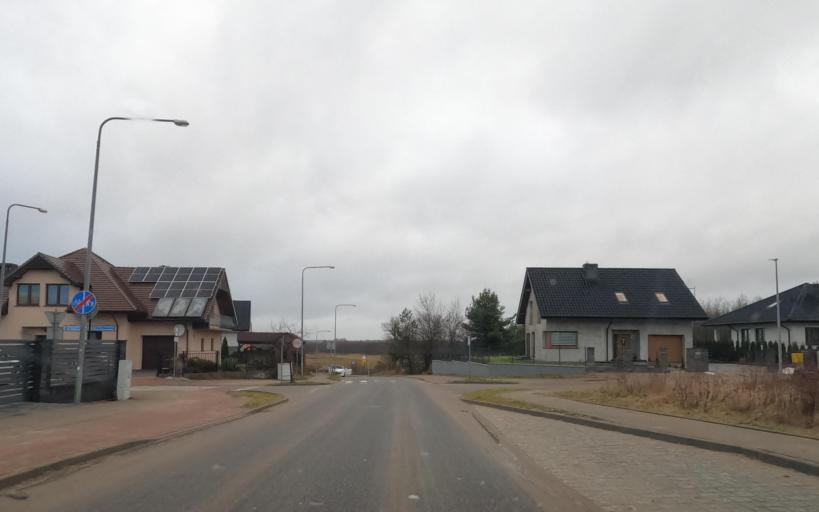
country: PL
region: West Pomeranian Voivodeship
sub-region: Powiat szczecinecki
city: Szczecinek
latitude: 53.7141
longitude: 16.7322
